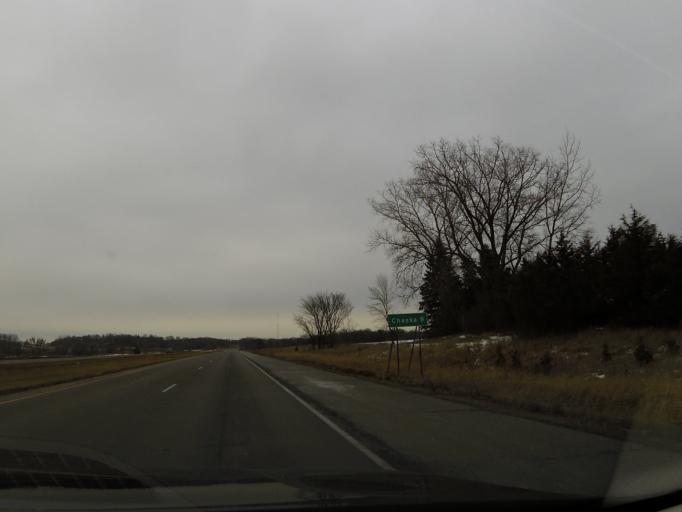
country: US
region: Minnesota
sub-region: Carver County
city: Cologne
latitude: 44.7670
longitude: -93.7738
